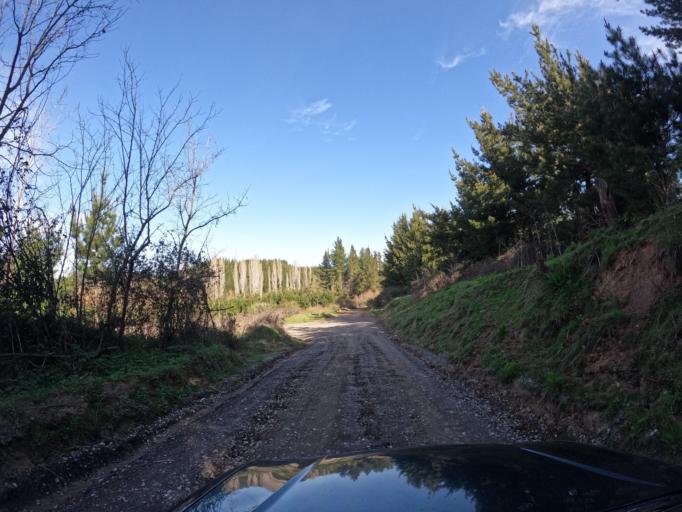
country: CL
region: Biobio
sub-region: Provincia de Biobio
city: La Laja
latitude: -37.0880
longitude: -72.7767
